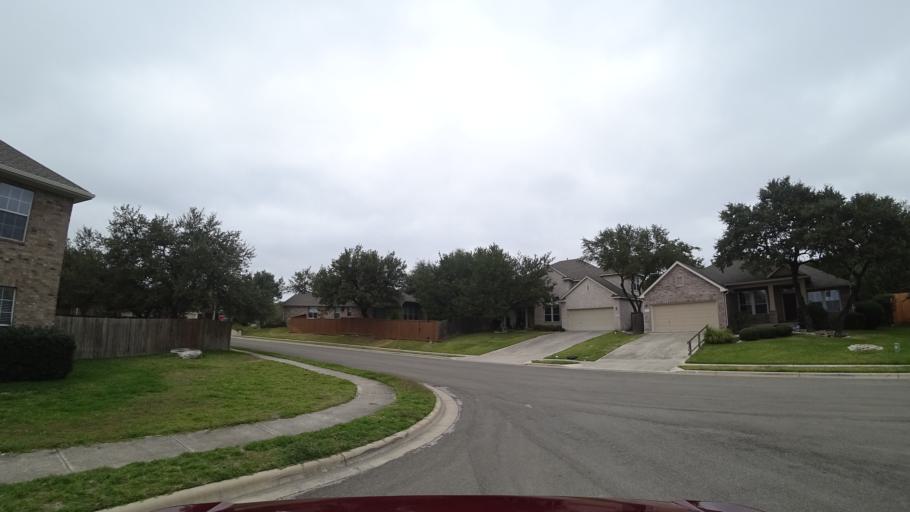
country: US
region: Texas
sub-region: Williamson County
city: Anderson Mill
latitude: 30.4375
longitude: -97.8304
